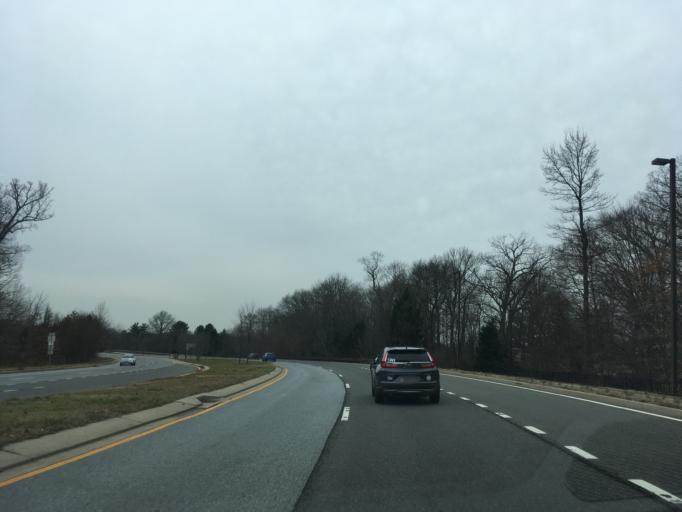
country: US
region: Delaware
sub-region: New Castle County
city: Wilmington
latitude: 39.7848
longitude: -75.5551
